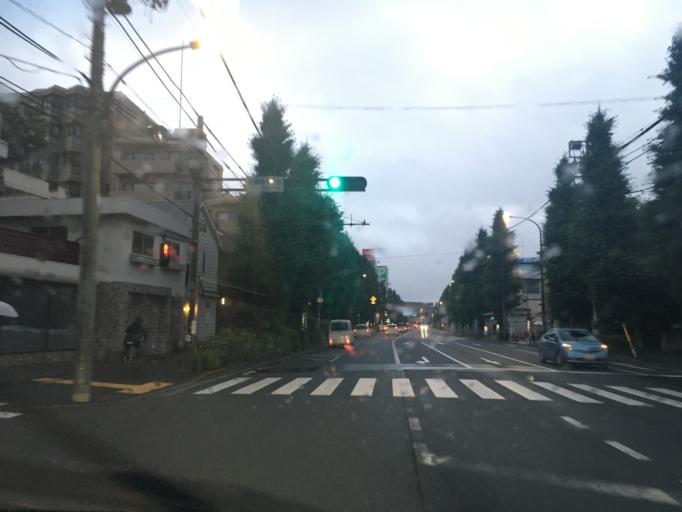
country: JP
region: Tokyo
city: Musashino
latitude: 35.7144
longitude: 139.5988
